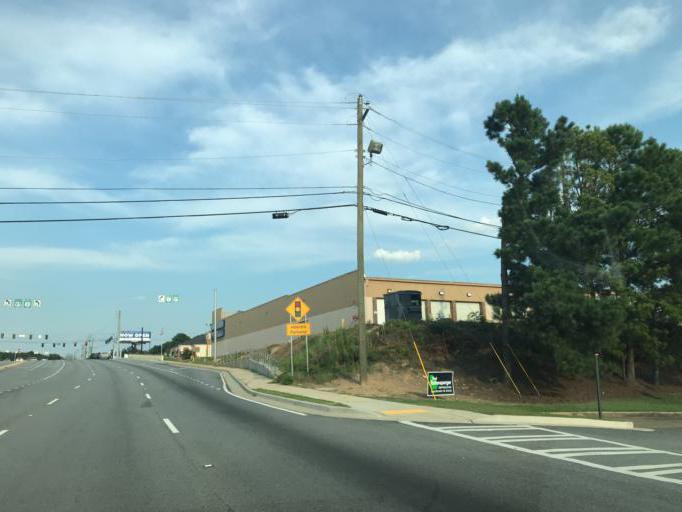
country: US
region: Alabama
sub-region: Russell County
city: Phenix City
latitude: 32.5394
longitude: -84.9570
